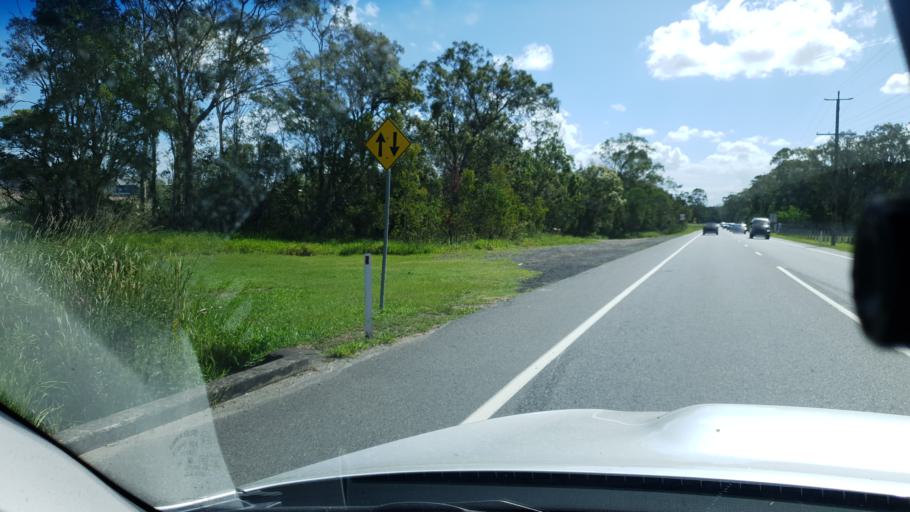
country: AU
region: Queensland
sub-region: Logan
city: Woodridge
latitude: -27.6462
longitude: 153.0920
